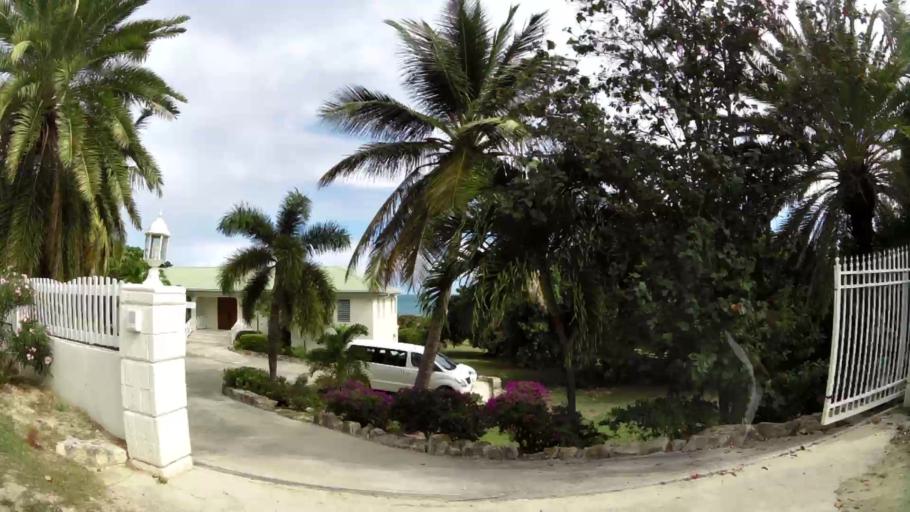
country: AG
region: Saint Peter
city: Parham
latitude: 17.0672
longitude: -61.6980
